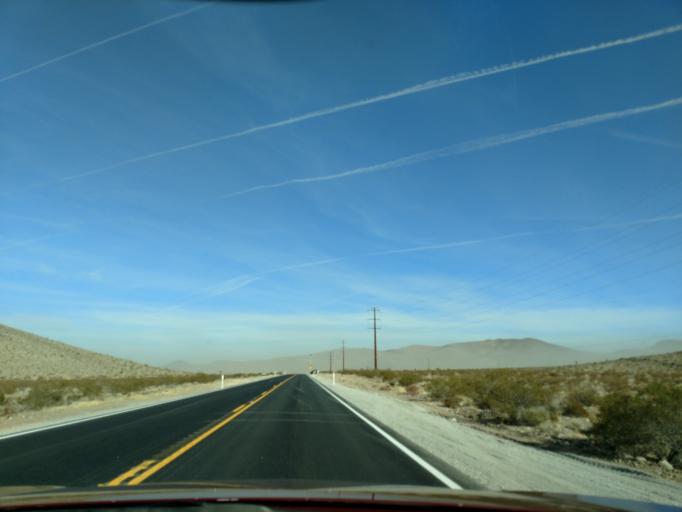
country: US
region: Nevada
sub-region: Nye County
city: Pahrump
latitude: 36.4263
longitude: -116.0708
